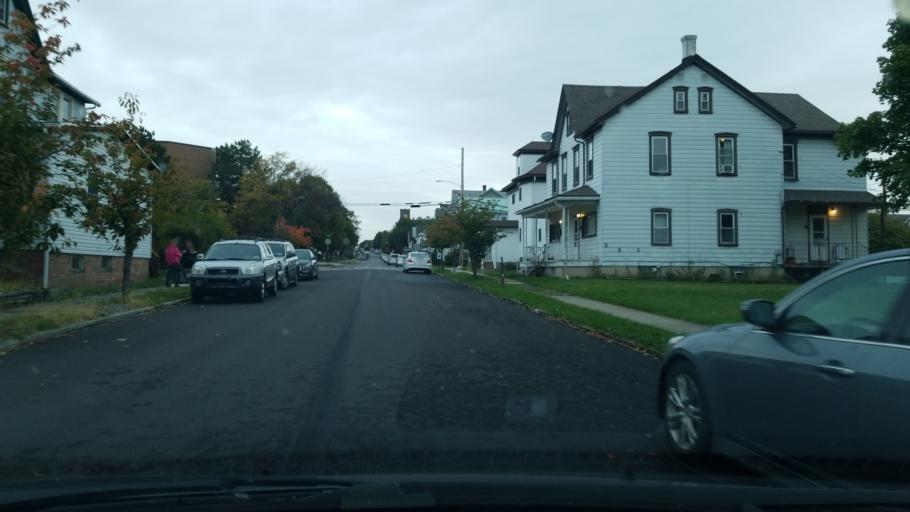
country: US
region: Pennsylvania
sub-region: Blair County
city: Altoona
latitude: 40.5363
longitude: -78.3871
